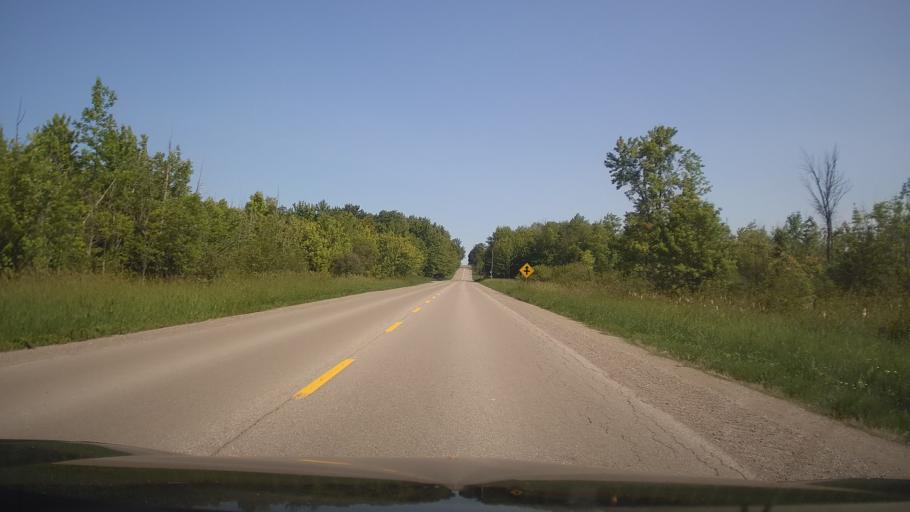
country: CA
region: Ontario
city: Uxbridge
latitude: 44.5222
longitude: -78.9612
